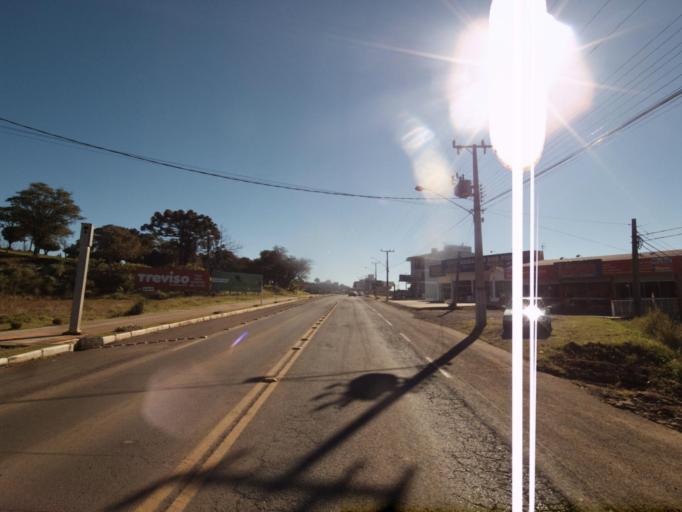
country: AR
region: Misiones
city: Bernardo de Irigoyen
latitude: -26.7505
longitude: -53.5154
